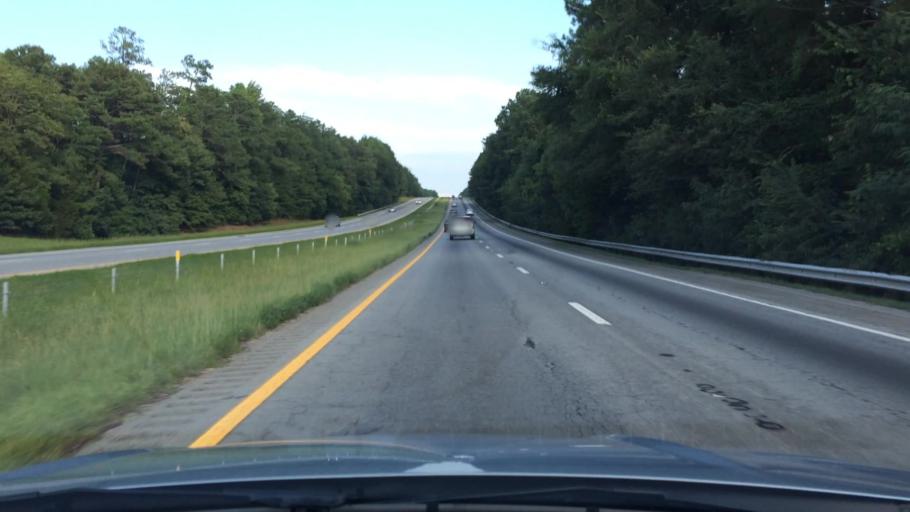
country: US
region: South Carolina
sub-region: Newberry County
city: Newberry
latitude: 34.3502
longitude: -81.6427
